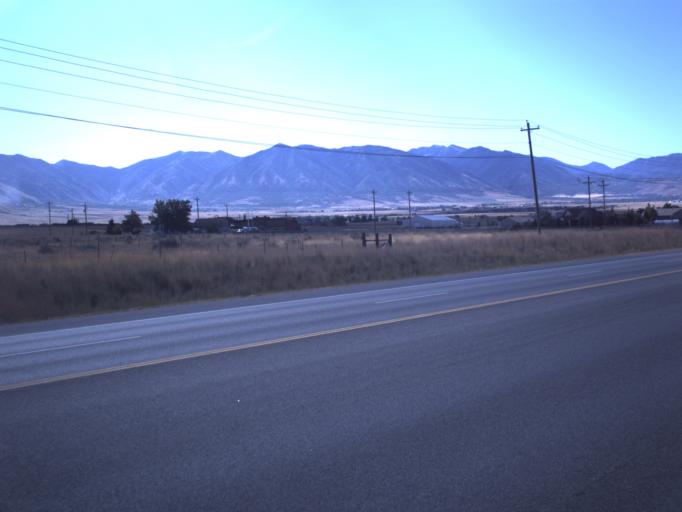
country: US
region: Utah
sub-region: Tooele County
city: Stansbury park
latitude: 40.6259
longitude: -112.2926
